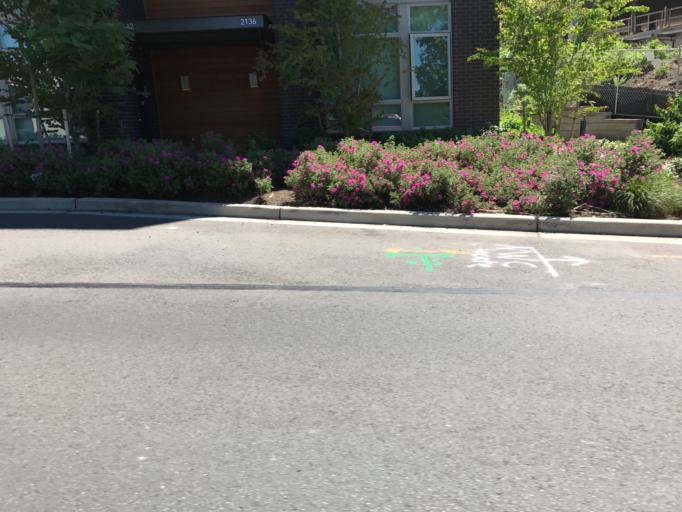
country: US
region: Washington
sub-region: King County
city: Redmond
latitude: 47.6293
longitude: -122.1349
